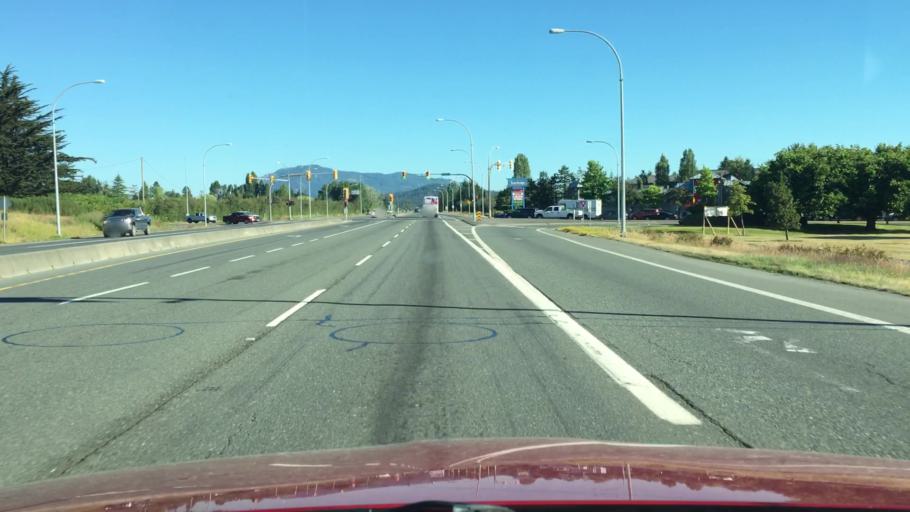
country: CA
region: British Columbia
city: North Saanich
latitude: 48.6479
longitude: -123.4063
